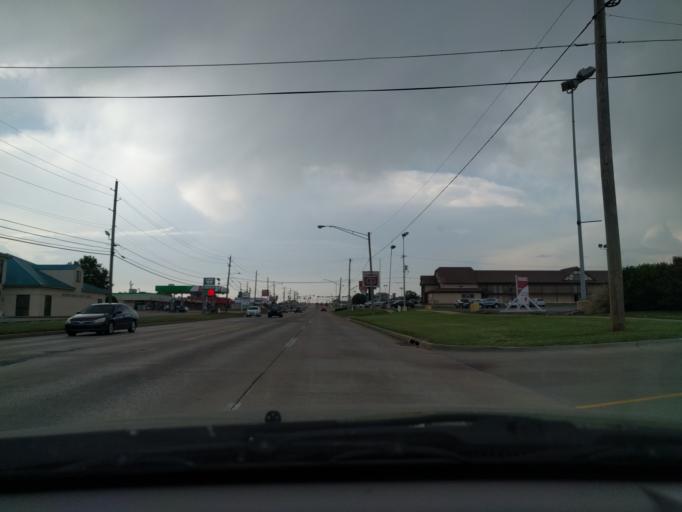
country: US
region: Oklahoma
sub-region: Tulsa County
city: Broken Arrow
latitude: 36.0663
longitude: -95.7974
